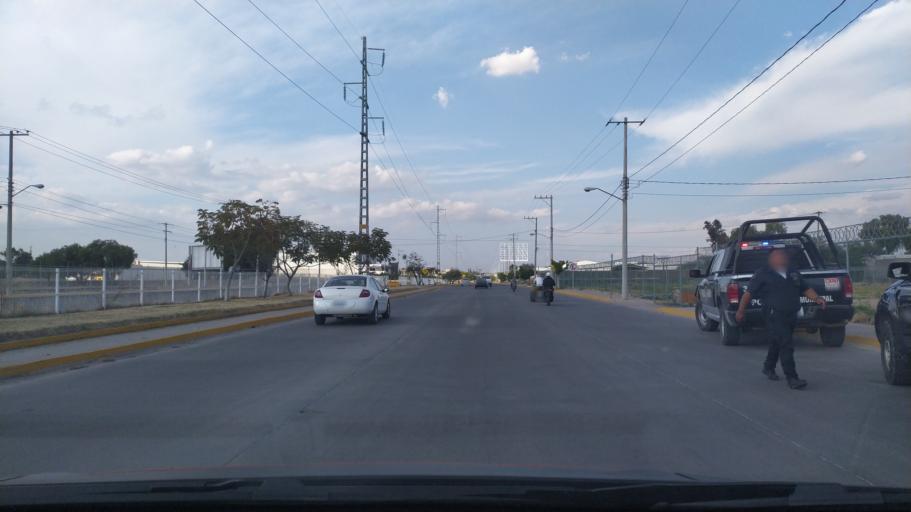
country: MX
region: Guanajuato
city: San Francisco del Rincon
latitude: 21.0191
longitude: -101.8696
